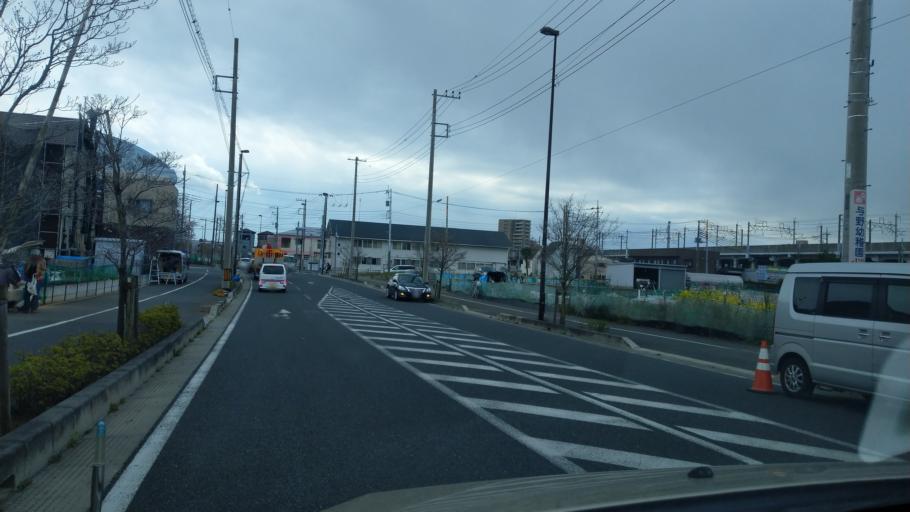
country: JP
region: Saitama
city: Yono
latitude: 35.8669
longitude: 139.6333
